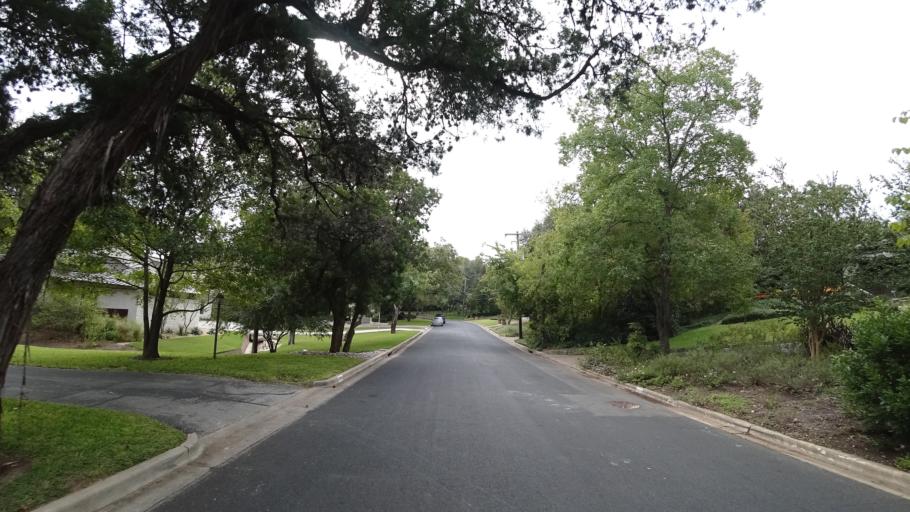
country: US
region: Texas
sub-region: Travis County
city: West Lake Hills
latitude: 30.3017
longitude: -97.7699
